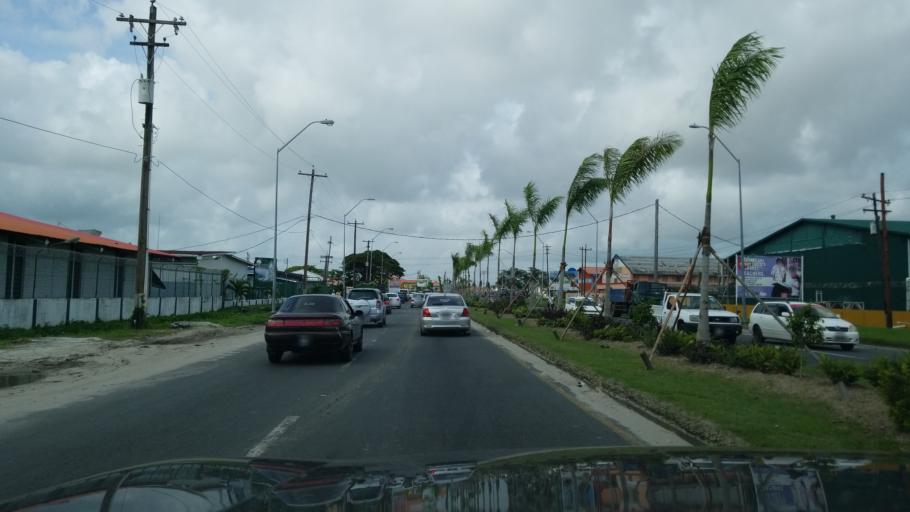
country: GY
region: Demerara-Mahaica
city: Georgetown
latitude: 6.7916
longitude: -58.1653
